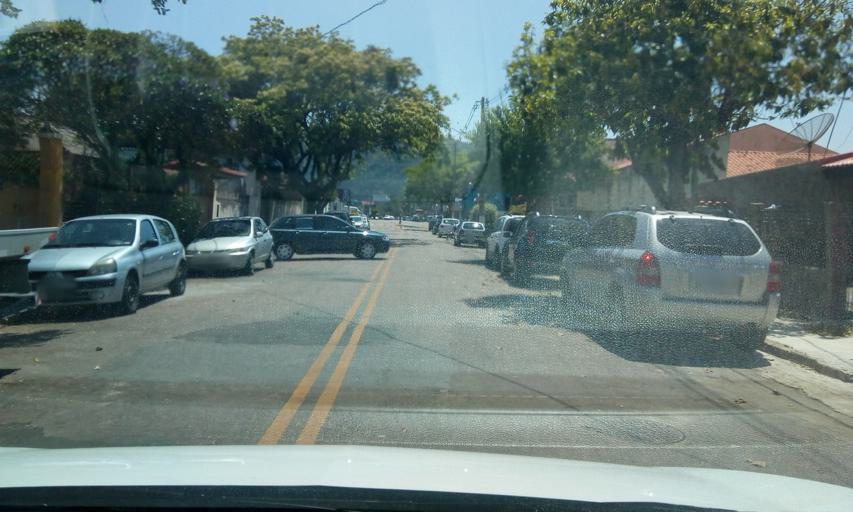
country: BR
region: Sao Paulo
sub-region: Itupeva
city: Itupeva
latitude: -23.1587
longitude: -47.0553
